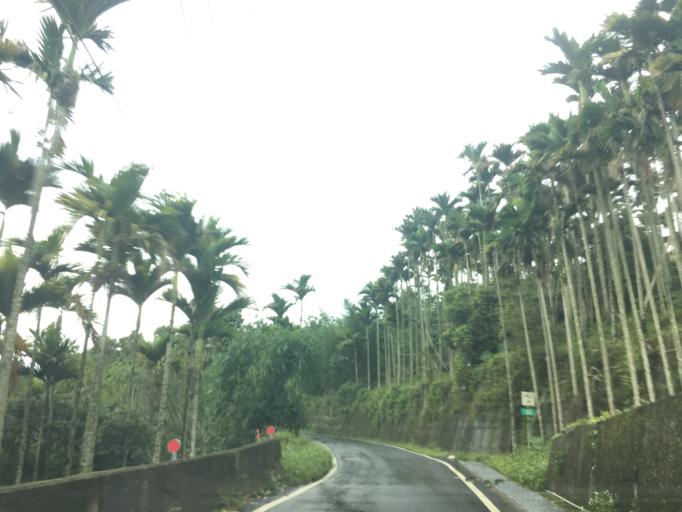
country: TW
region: Taiwan
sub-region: Yunlin
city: Douliu
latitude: 23.5596
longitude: 120.6564
